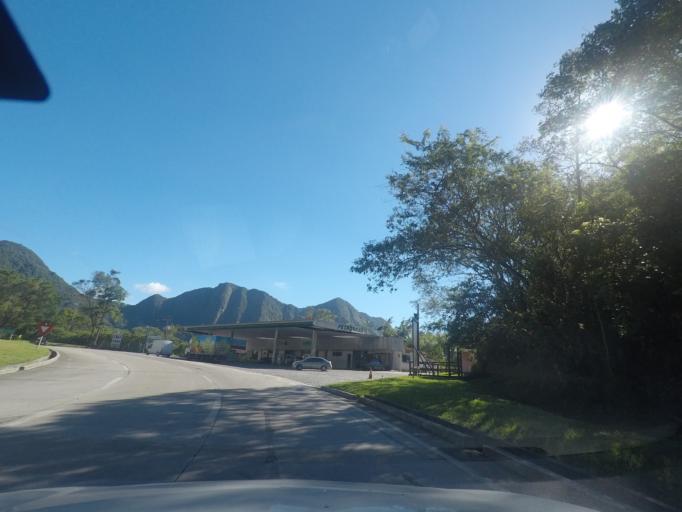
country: BR
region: Rio de Janeiro
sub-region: Guapimirim
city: Guapimirim
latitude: -22.4820
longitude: -42.9965
